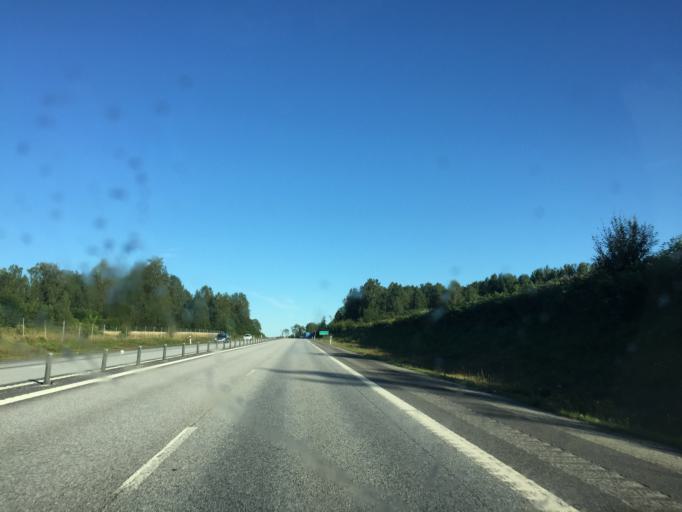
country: SE
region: OErebro
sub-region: Orebro Kommun
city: Vintrosa
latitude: 59.2507
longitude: 14.9207
